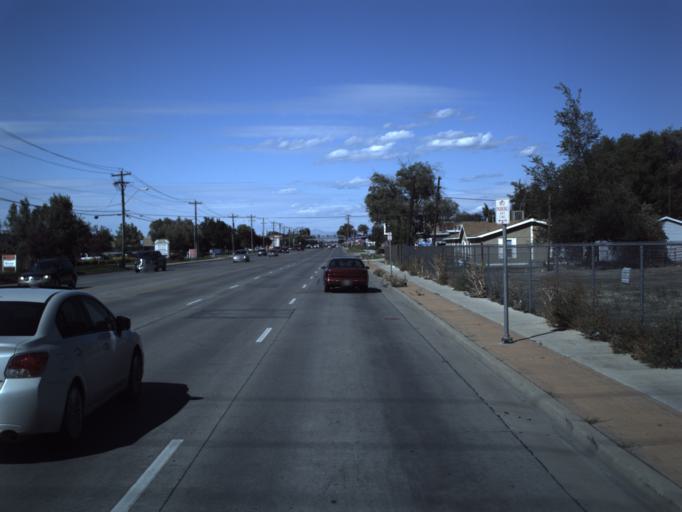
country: US
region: Utah
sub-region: Salt Lake County
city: Taylorsville
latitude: 40.7070
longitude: -111.9388
